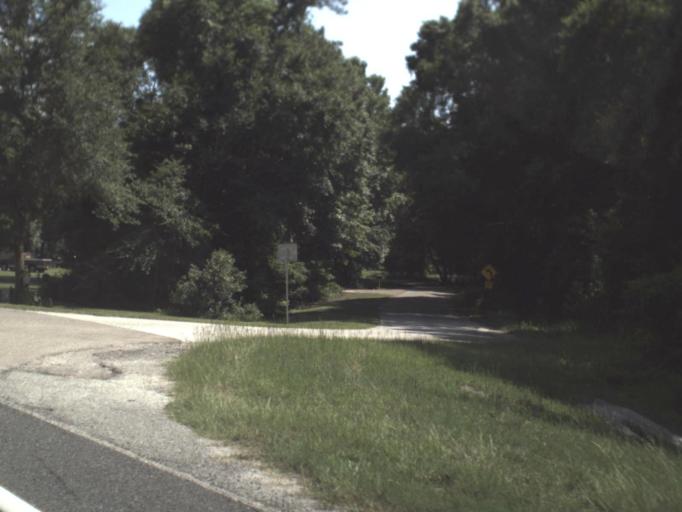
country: US
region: Florida
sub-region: Alachua County
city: Waldo
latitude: 29.7211
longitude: -82.1409
